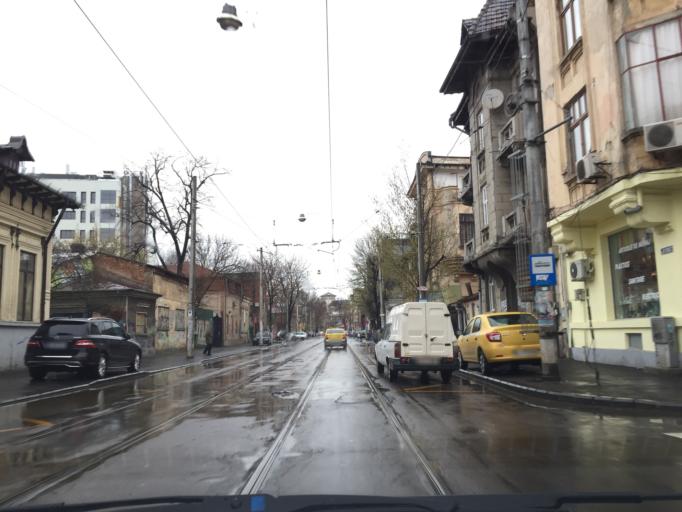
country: RO
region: Bucuresti
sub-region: Municipiul Bucuresti
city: Bucuresti
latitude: 44.4195
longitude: 26.0950
